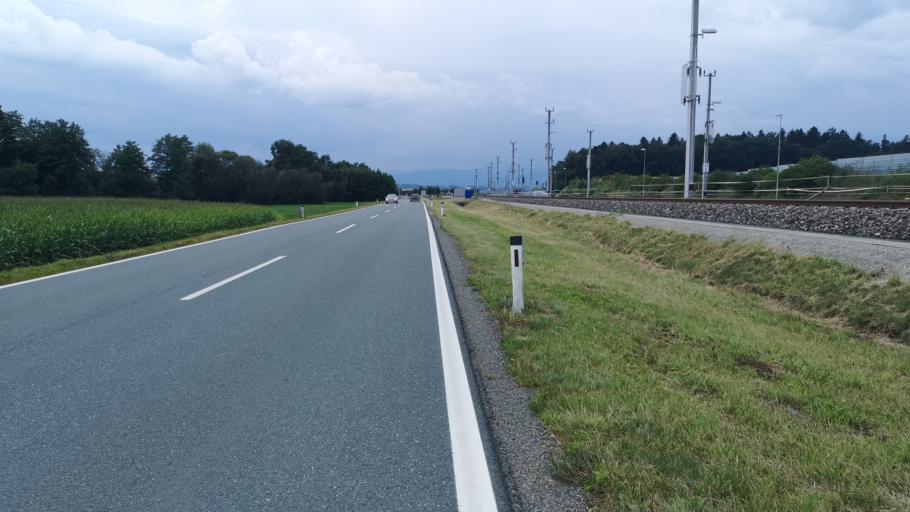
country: AT
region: Styria
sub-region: Politischer Bezirk Deutschlandsberg
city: Wettmannstatten
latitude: 46.8393
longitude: 15.3873
